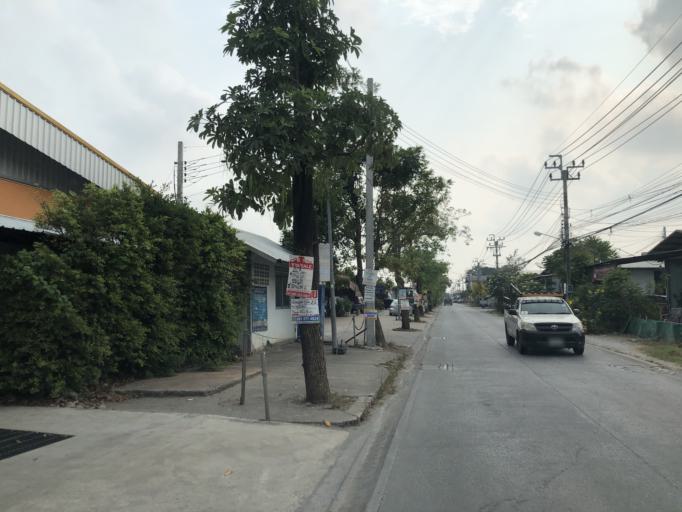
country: TH
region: Bangkok
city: Bang Na
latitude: 13.5863
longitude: 100.6992
